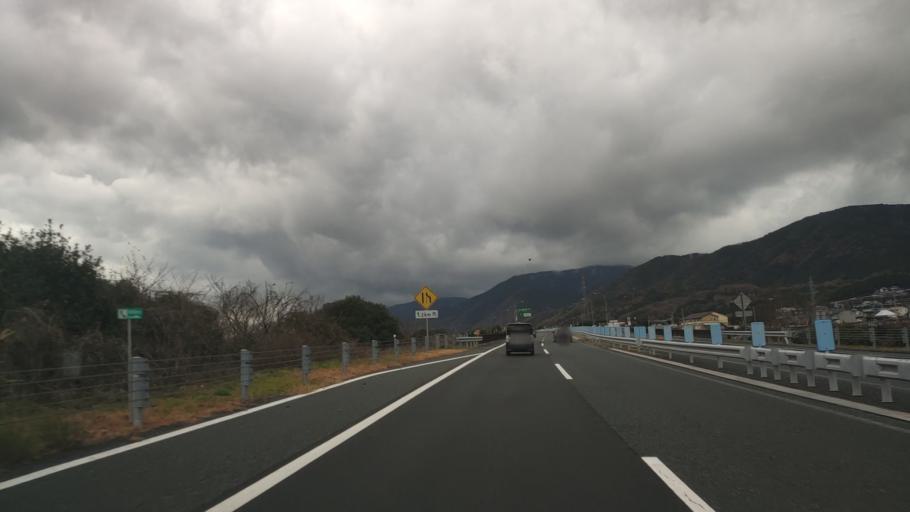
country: JP
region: Tokushima
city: Ikedacho
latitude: 34.0369
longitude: 133.8996
